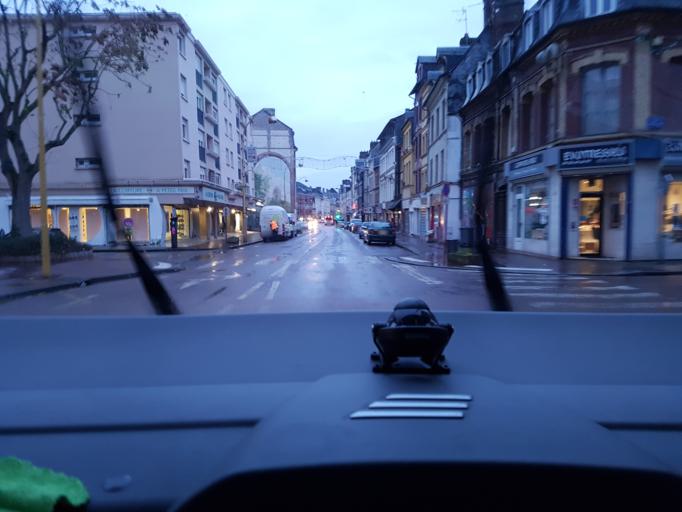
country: FR
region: Haute-Normandie
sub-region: Departement de la Seine-Maritime
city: Elbeuf
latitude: 49.2908
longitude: 1.0009
